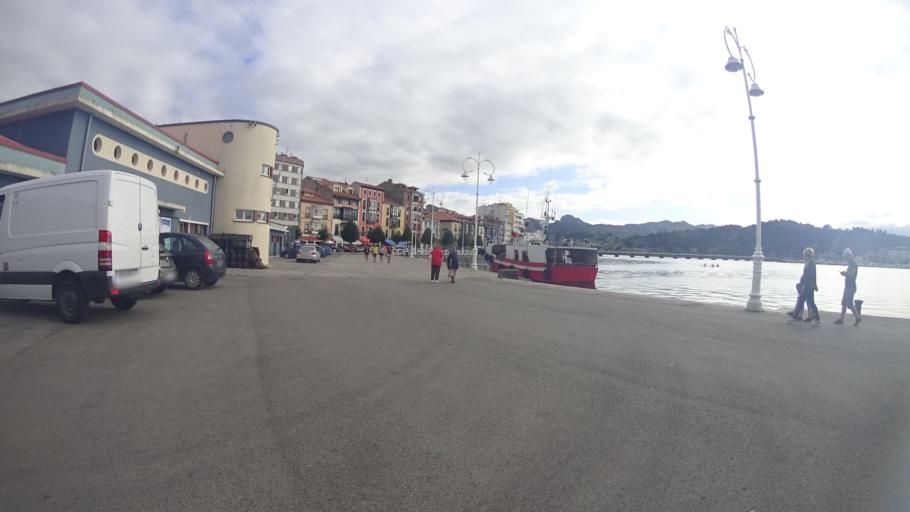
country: ES
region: Asturias
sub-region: Province of Asturias
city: Ribadesella
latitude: 43.4640
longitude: -5.0586
